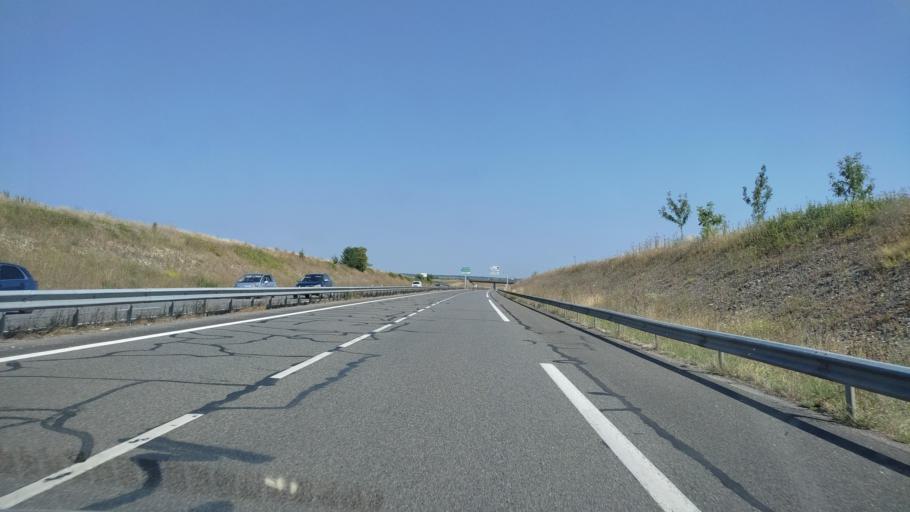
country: FR
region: Poitou-Charentes
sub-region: Departement de la Charente
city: Saint-Meme-les-Carrieres
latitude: 45.6929
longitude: -0.0938
